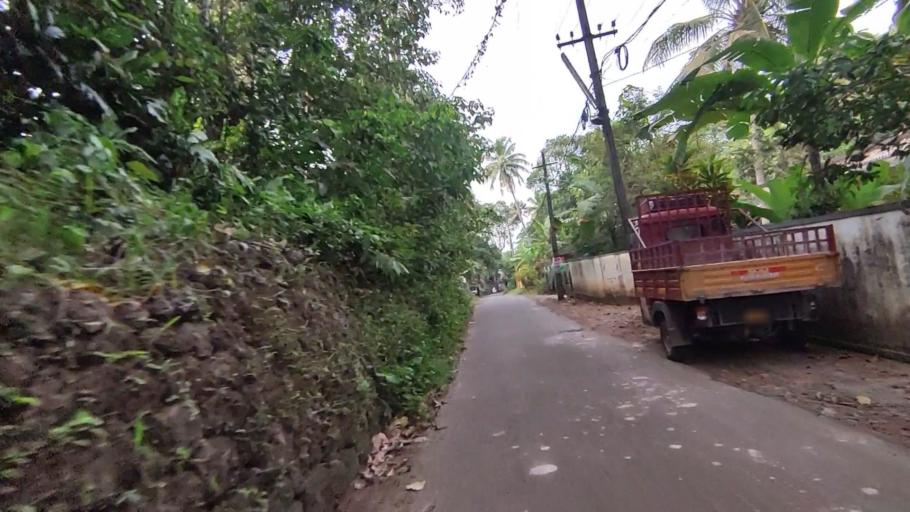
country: IN
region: Kerala
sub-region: Kottayam
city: Kottayam
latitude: 9.6096
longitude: 76.4849
